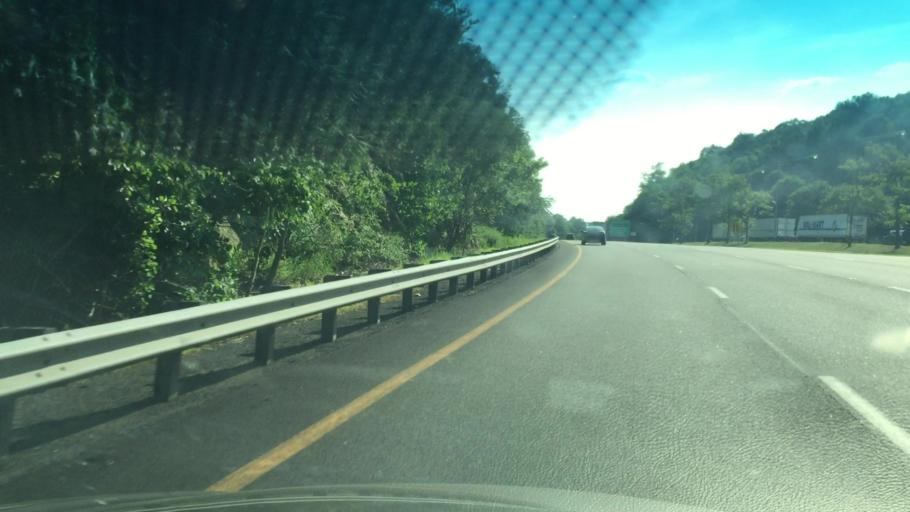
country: US
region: New Jersey
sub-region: Morris County
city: Budd Lake
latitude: 40.9253
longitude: -74.7899
